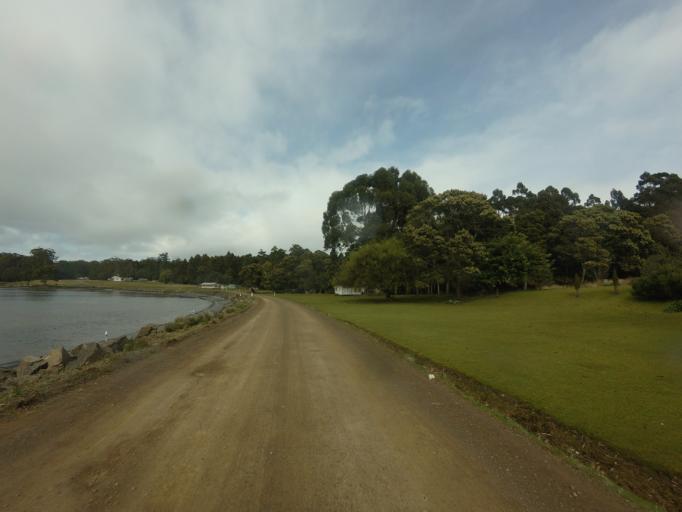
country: AU
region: Tasmania
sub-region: Huon Valley
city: Geeveston
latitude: -43.5344
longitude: 146.8907
